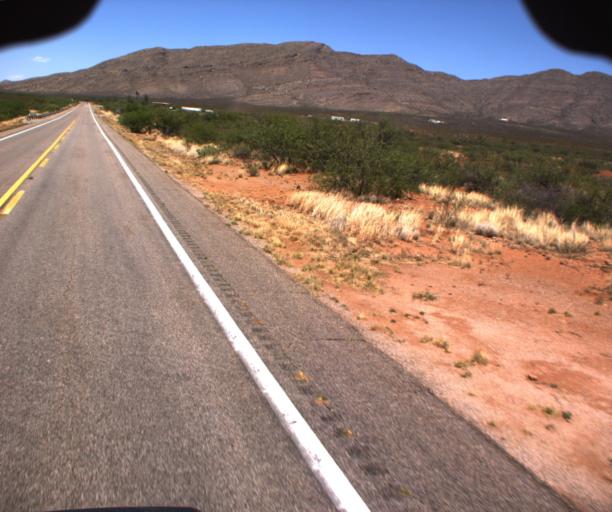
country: US
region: Arizona
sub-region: Cochise County
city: Tombstone
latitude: 31.5682
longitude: -110.0268
